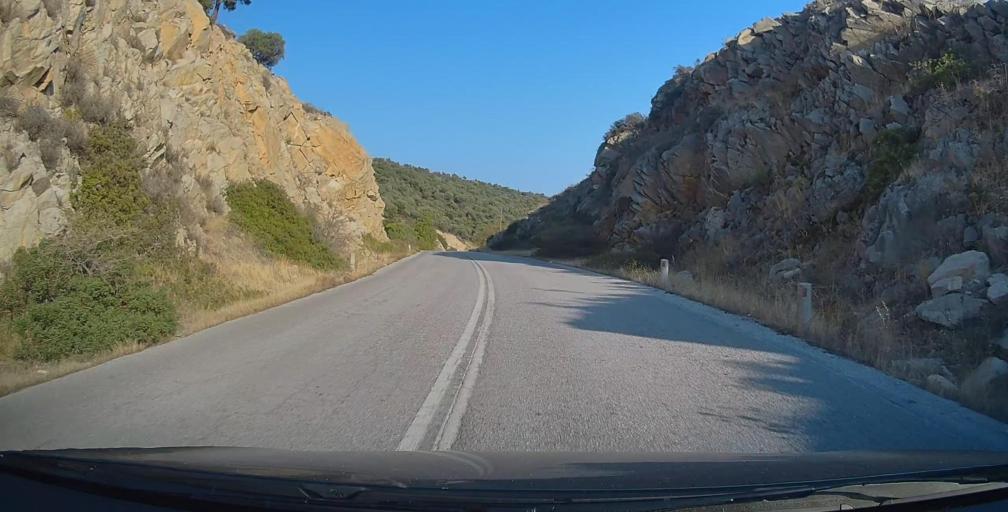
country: GR
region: Central Macedonia
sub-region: Nomos Chalkidikis
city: Sykia
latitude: 40.0094
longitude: 23.8756
